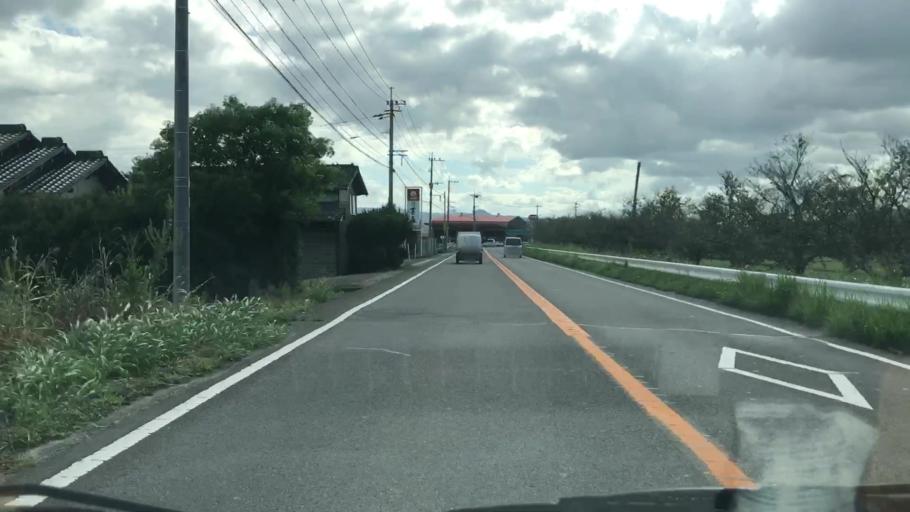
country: JP
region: Saga Prefecture
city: Kashima
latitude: 33.1546
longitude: 130.1571
